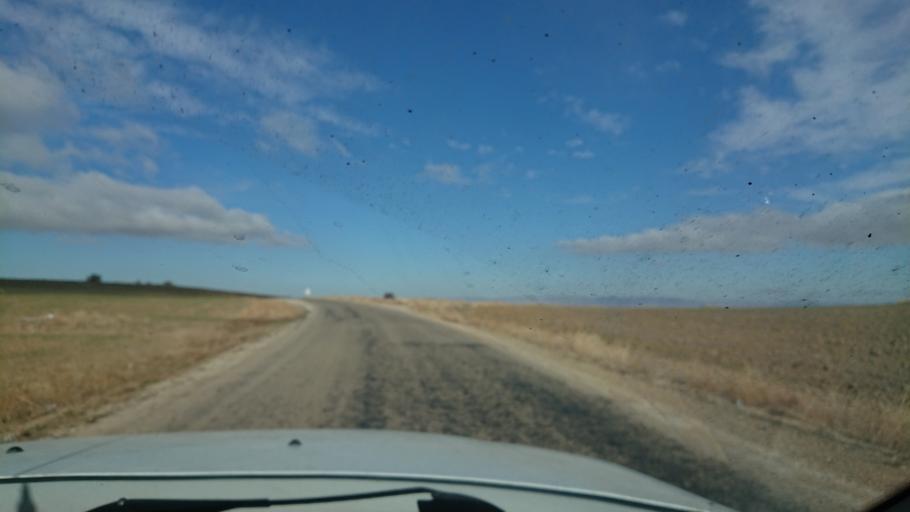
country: TR
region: Aksaray
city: Agacoren
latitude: 38.8387
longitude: 33.9537
